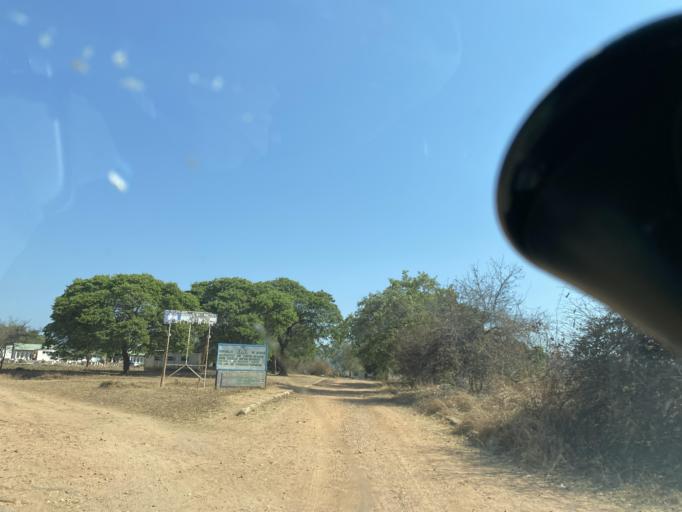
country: ZM
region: Lusaka
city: Chongwe
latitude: -15.2138
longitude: 28.8342
